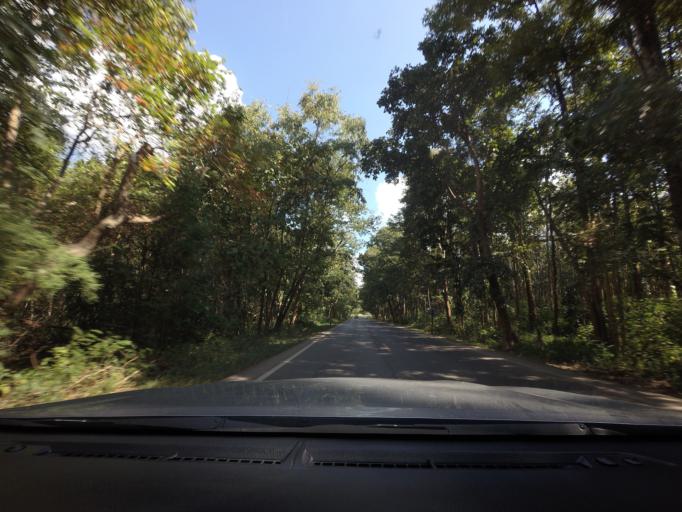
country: TH
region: Chiang Mai
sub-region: Amphoe Chiang Dao
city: Chiang Dao
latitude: 19.4972
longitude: 99.0388
